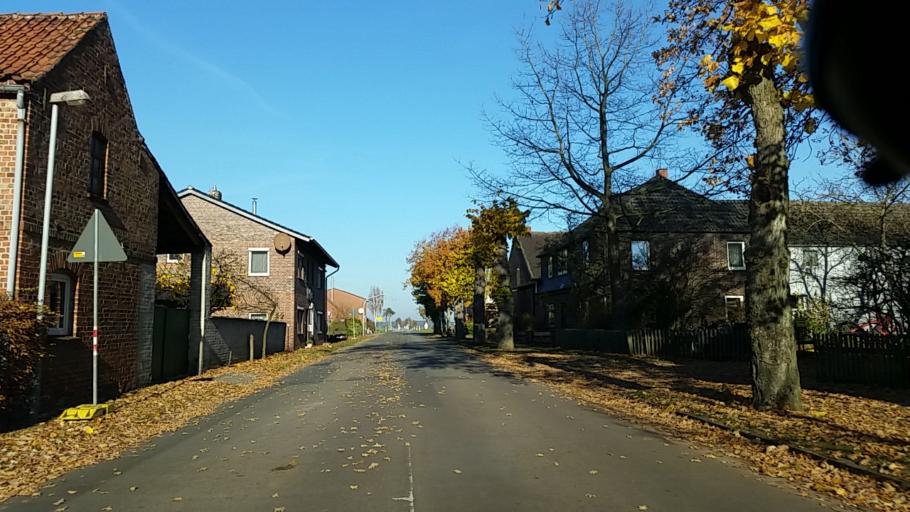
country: DE
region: Lower Saxony
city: Tulau
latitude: 52.5927
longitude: 10.8822
